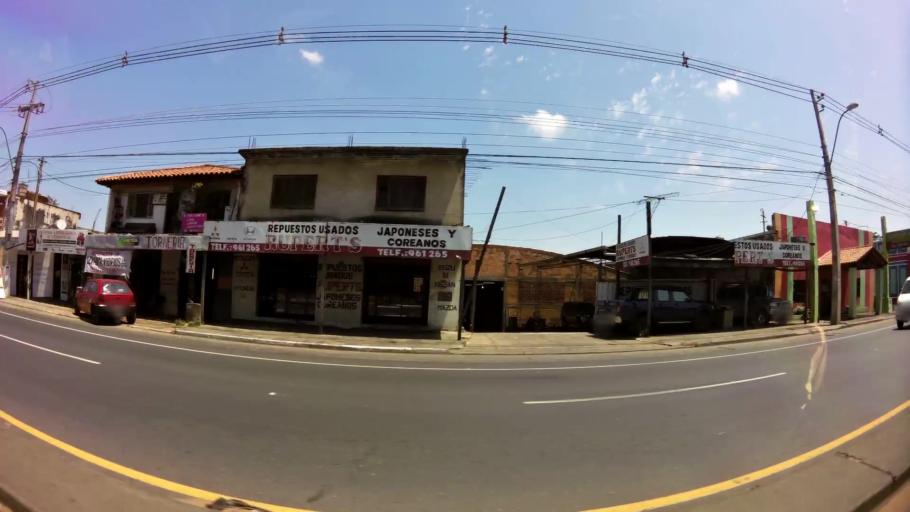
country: PY
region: Central
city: Nemby
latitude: -25.3750
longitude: -57.5566
